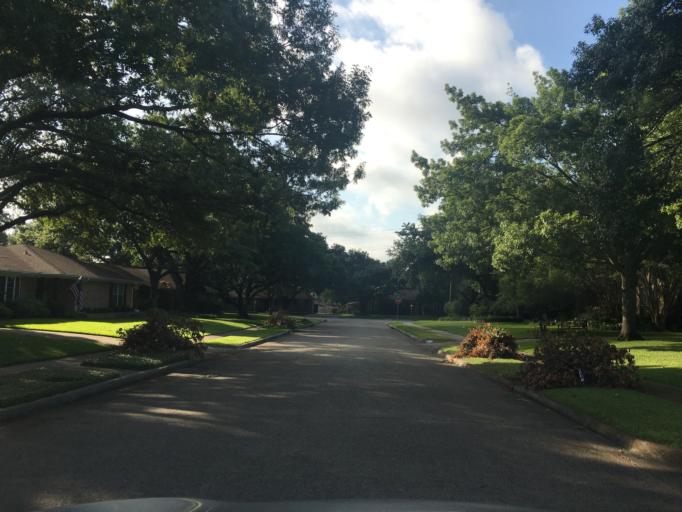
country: US
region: Texas
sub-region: Dallas County
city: Highland Park
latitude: 32.8450
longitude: -96.7546
